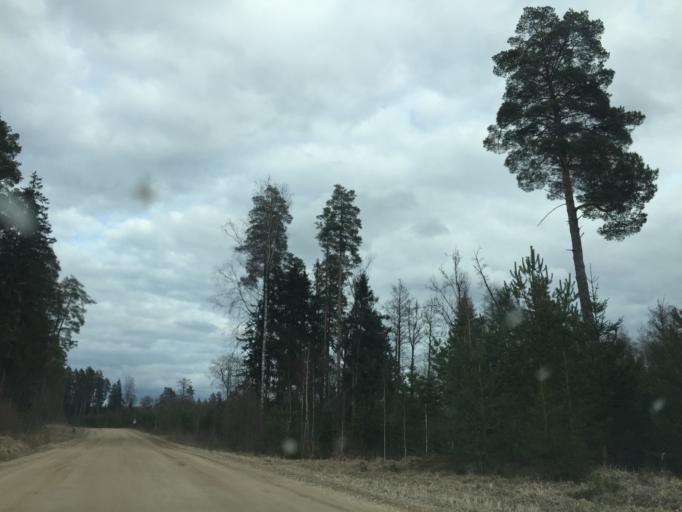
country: LV
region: Lielvarde
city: Lielvarde
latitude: 56.5418
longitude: 24.8389
